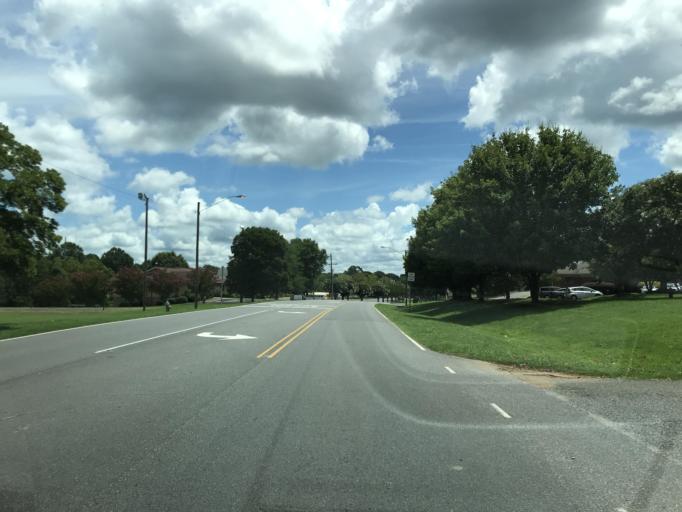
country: US
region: North Carolina
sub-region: Cleveland County
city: Shelby
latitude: 35.3023
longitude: -81.5104
